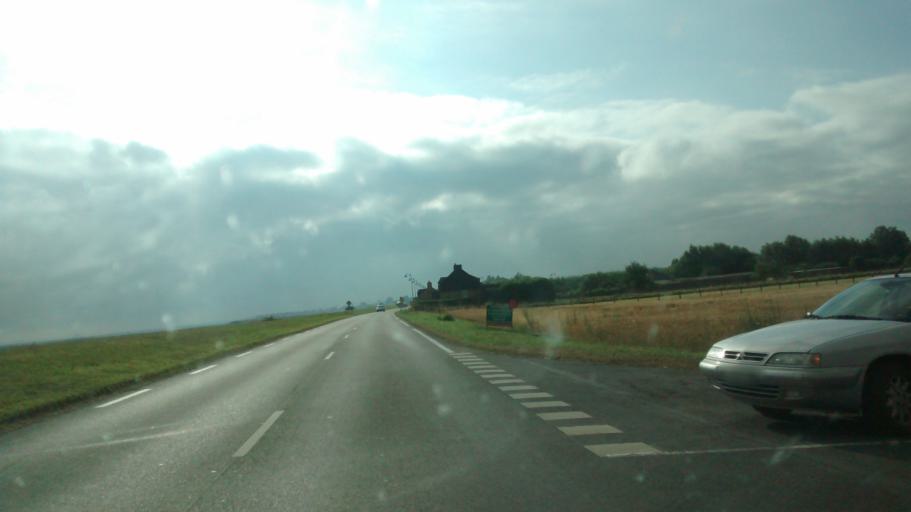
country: FR
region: Brittany
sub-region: Departement d'Ille-et-Vilaine
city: Hirel
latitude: 48.6059
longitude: -1.7912
